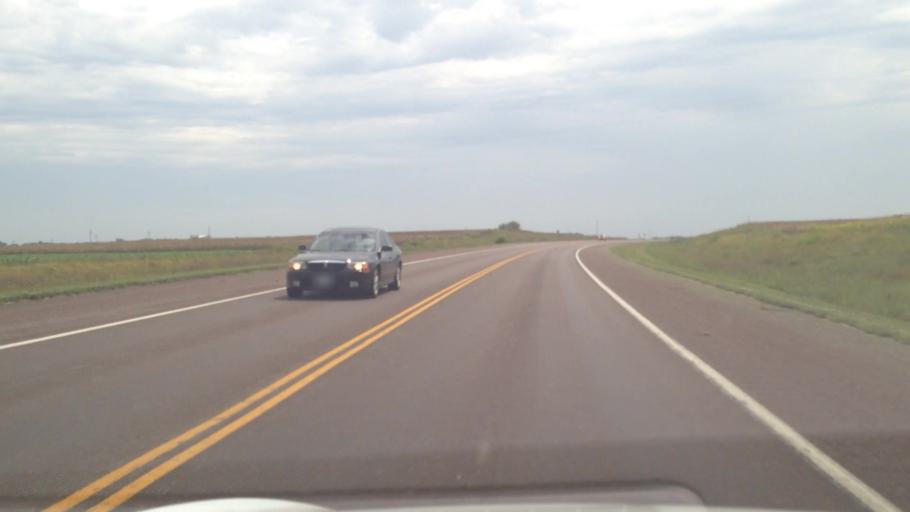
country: US
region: Kansas
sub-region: Crawford County
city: Girard
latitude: 37.4735
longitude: -94.8371
